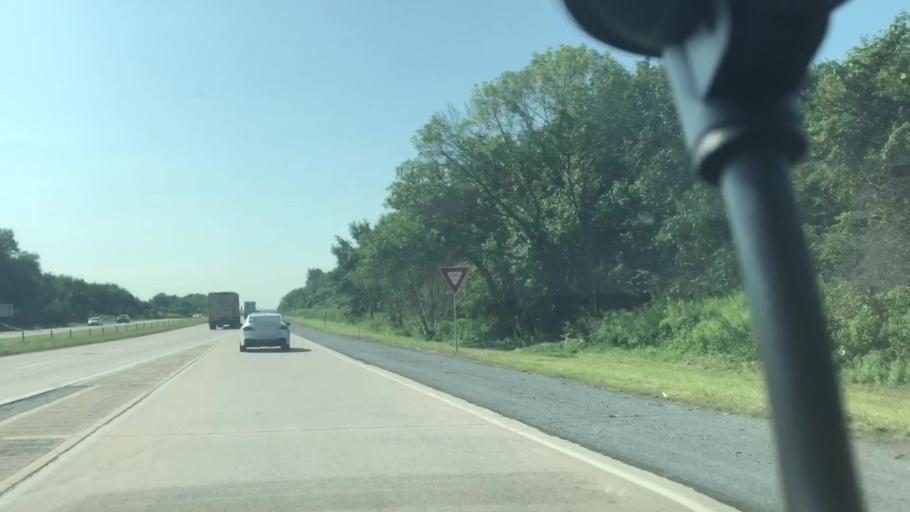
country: US
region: Pennsylvania
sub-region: Montgomery County
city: Limerick
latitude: 40.2141
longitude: -75.5428
